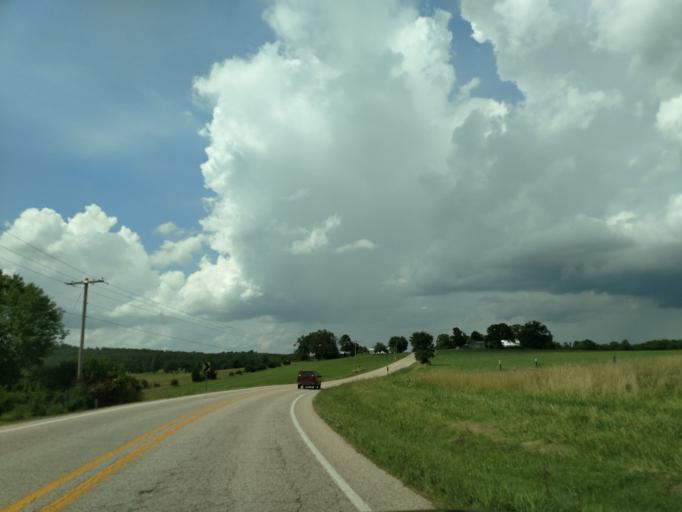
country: US
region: Arkansas
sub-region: Boone County
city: Harrison
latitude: 36.2737
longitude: -93.2343
